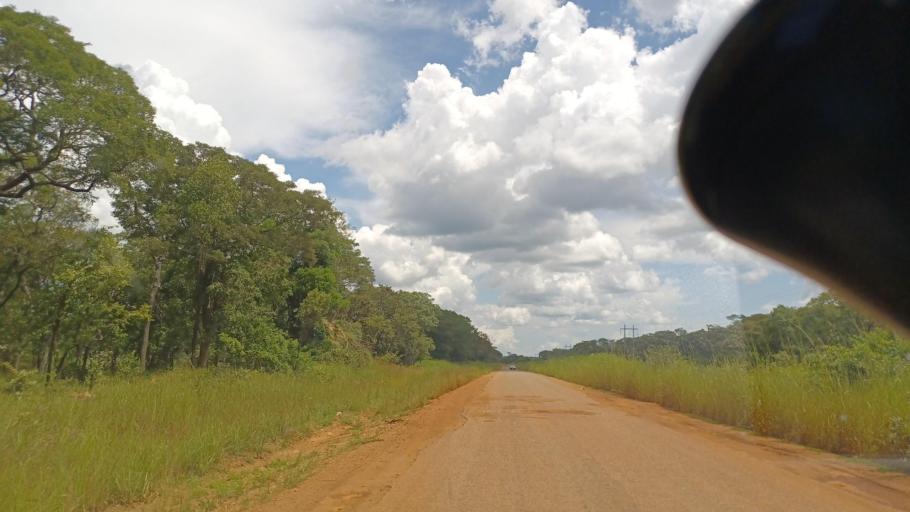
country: ZM
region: North-Western
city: Solwezi
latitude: -12.7107
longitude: 26.0265
